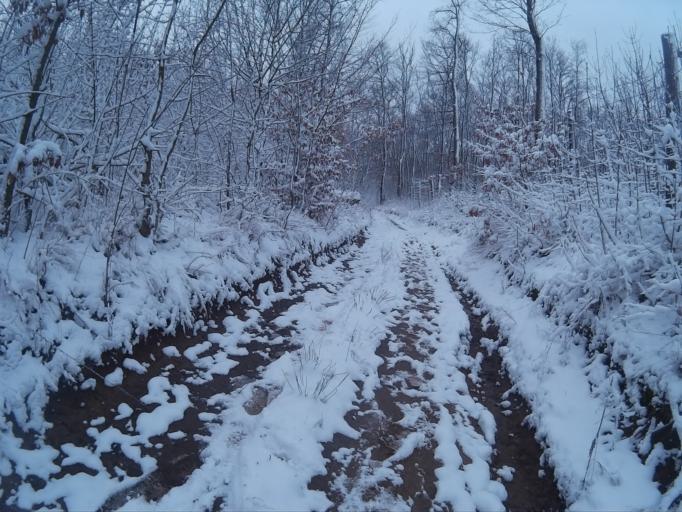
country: HU
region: Fejer
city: Szarliget
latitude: 47.5150
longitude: 18.5095
